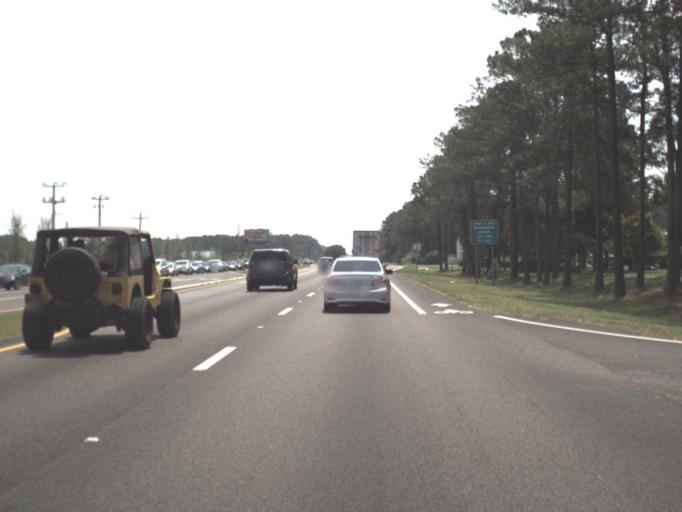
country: US
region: Florida
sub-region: Nassau County
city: Yulee
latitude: 30.6257
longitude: -81.5465
